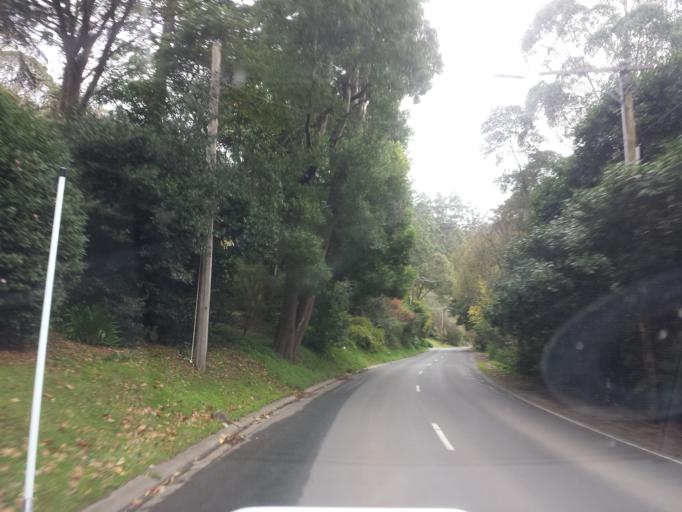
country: AU
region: Victoria
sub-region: Yarra Ranges
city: Monbulk
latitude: -37.8916
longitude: 145.3894
